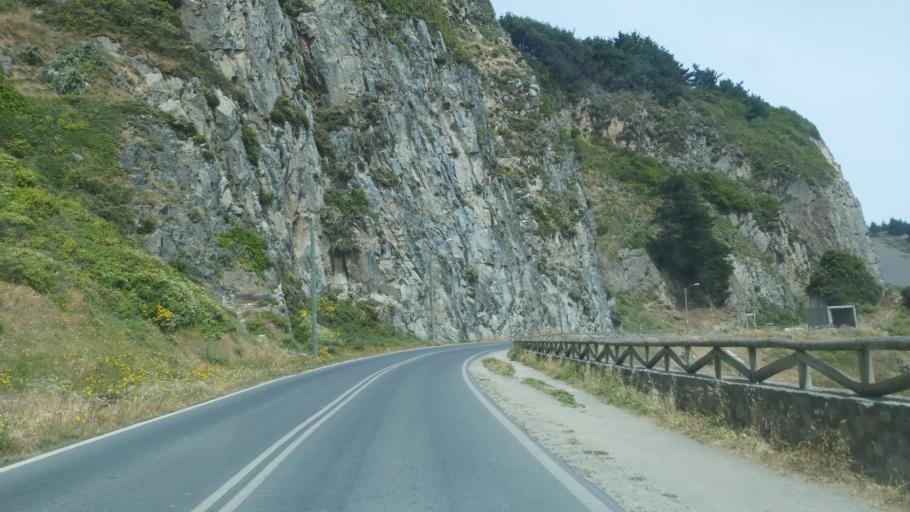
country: CL
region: Maule
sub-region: Provincia de Talca
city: Constitucion
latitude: -35.3318
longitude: -72.4340
